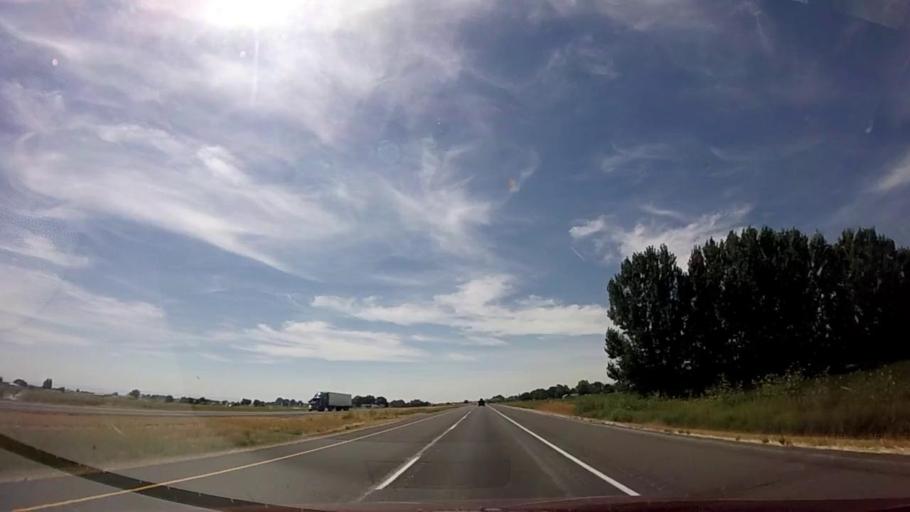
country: US
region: Idaho
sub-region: Minidoka County
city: Rupert
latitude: 42.5690
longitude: -113.6825
